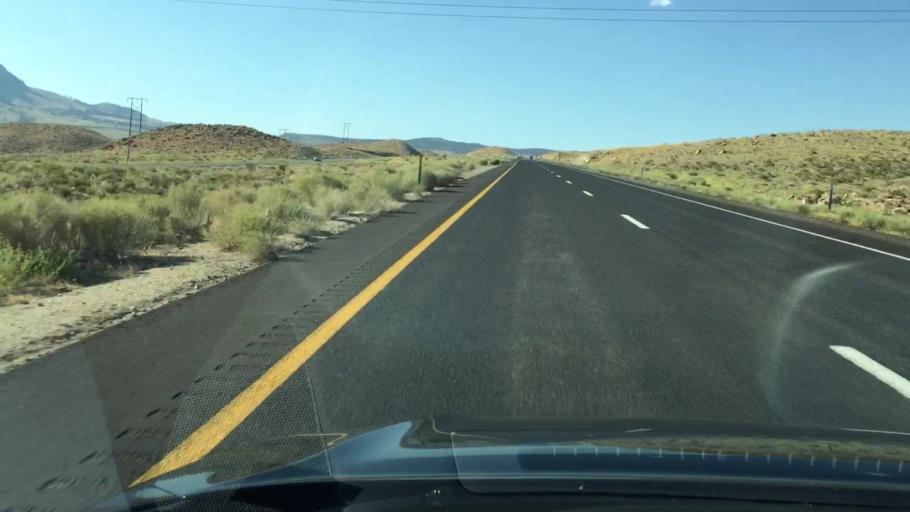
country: US
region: California
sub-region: Inyo County
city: West Bishop
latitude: 37.4562
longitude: -118.5750
